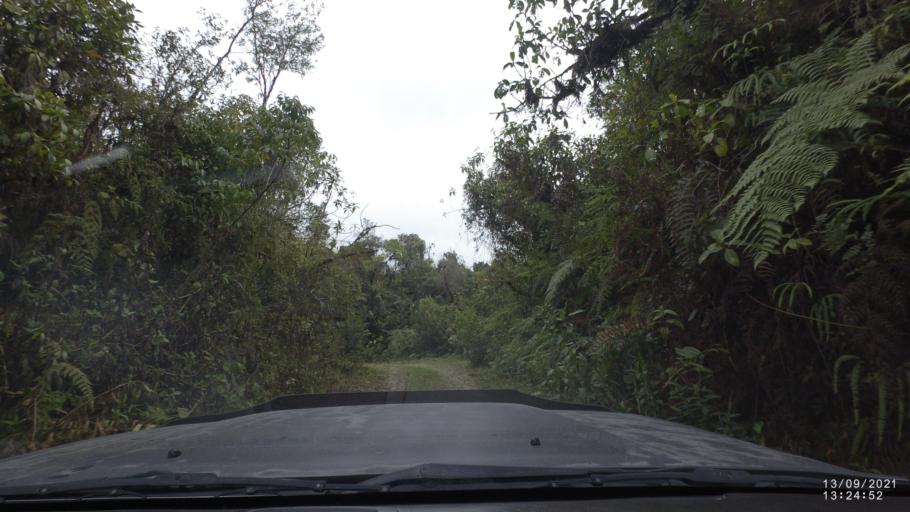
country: BO
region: Cochabamba
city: Colomi
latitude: -17.2115
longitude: -65.8652
